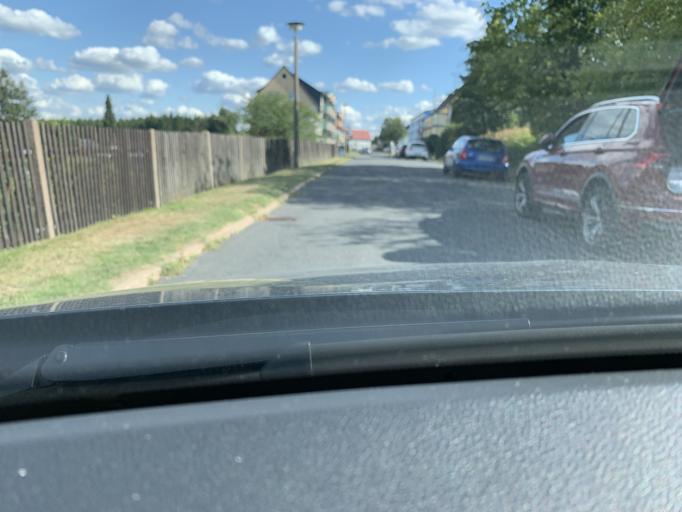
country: DE
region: Thuringia
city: Neuhaus am Rennweg
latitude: 50.5061
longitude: 11.1479
